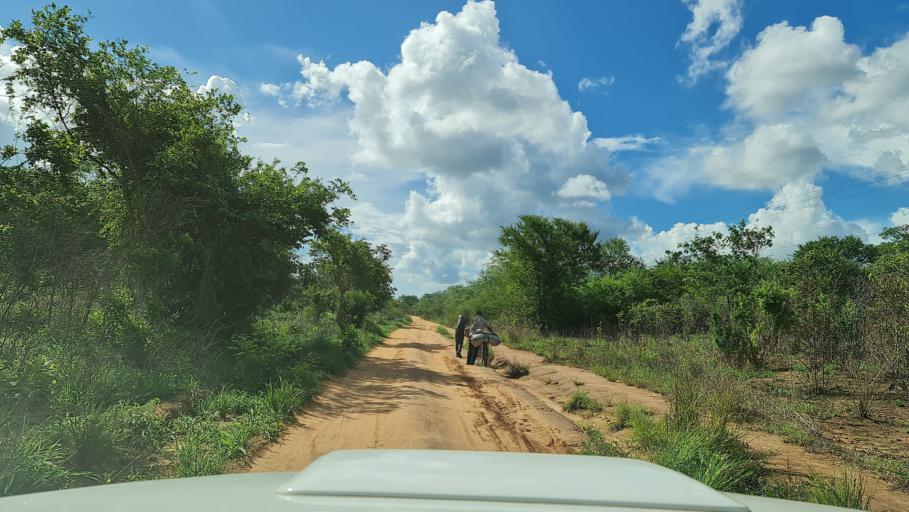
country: MZ
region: Nampula
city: Ilha de Mocambique
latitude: -15.4144
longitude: 40.2568
